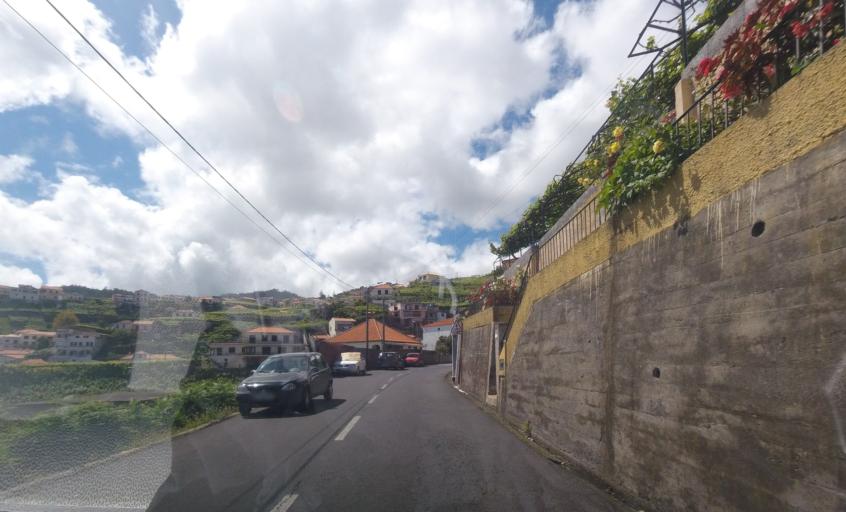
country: PT
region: Madeira
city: Camara de Lobos
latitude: 32.6742
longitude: -16.9754
